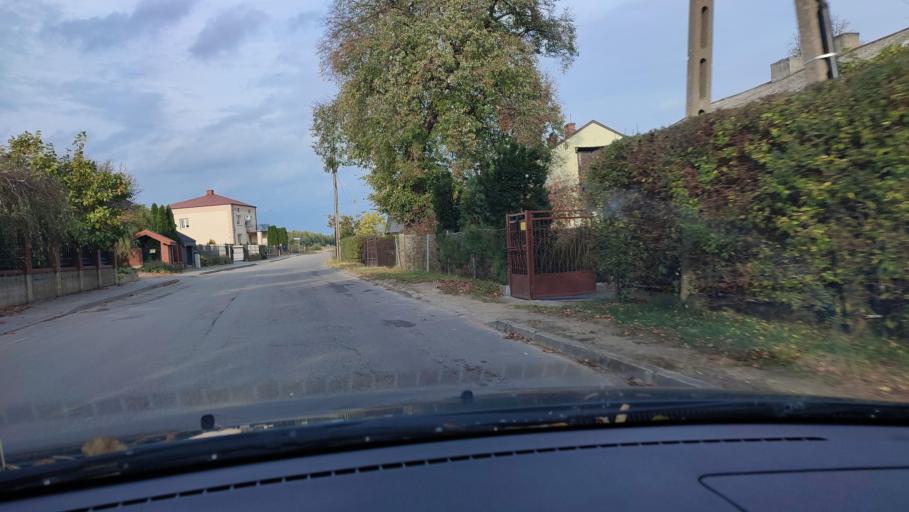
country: PL
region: Masovian Voivodeship
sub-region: Powiat mlawski
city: Mlawa
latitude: 53.1371
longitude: 20.3653
